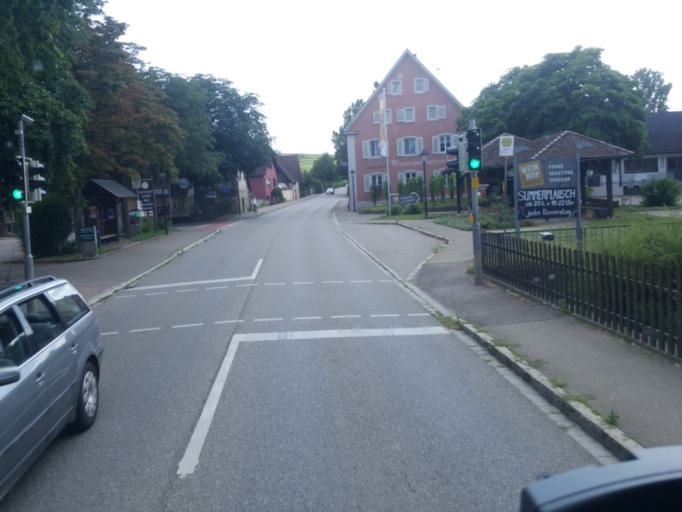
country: DE
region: Baden-Wuerttemberg
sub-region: Freiburg Region
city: Mullheim
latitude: 47.8299
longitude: 7.6209
